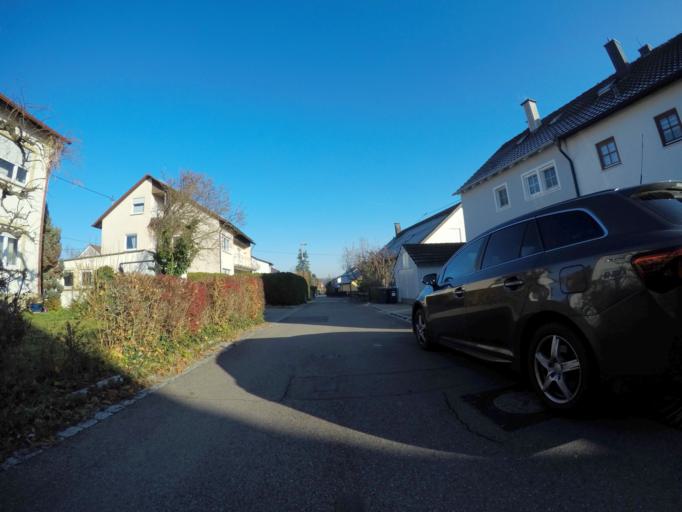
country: DE
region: Baden-Wuerttemberg
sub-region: Tuebingen Region
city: Reutlingen
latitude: 48.5162
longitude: 9.2210
